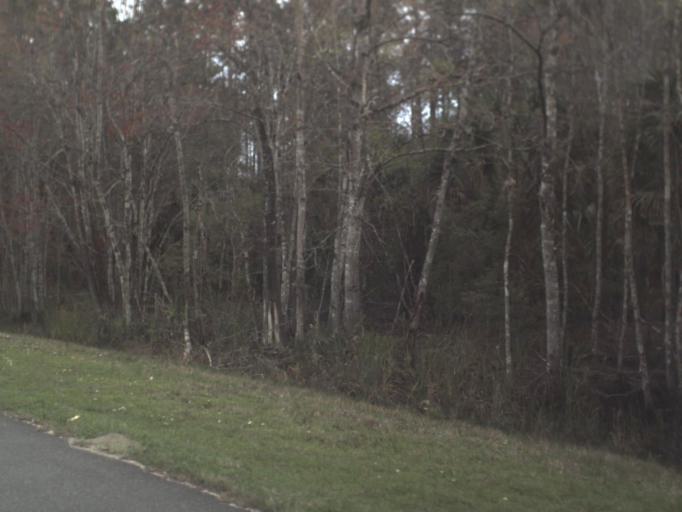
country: US
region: Florida
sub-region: Leon County
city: Woodville
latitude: 30.1711
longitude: -84.0076
